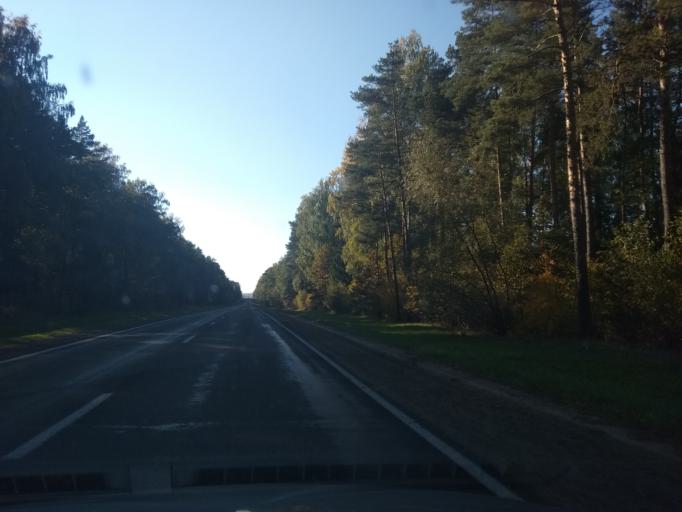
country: BY
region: Grodnenskaya
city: Vawkavysk
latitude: 53.1467
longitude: 24.5203
